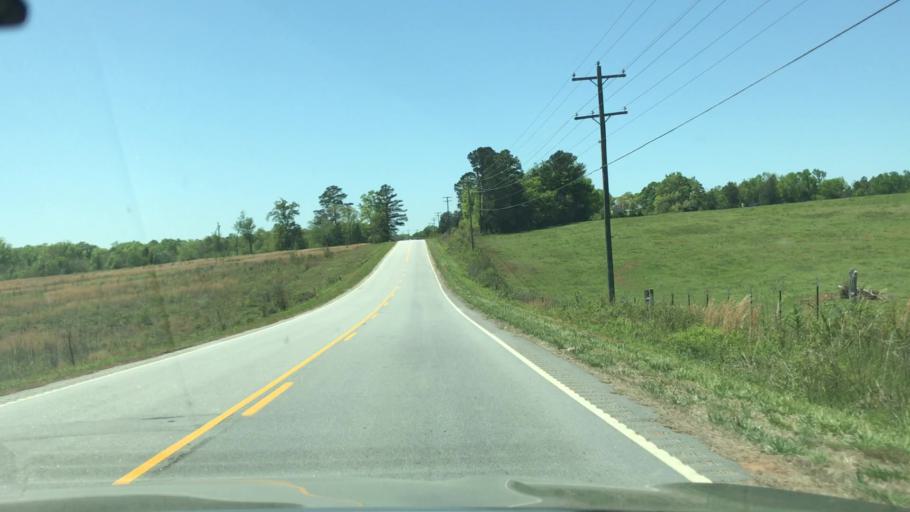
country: US
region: South Carolina
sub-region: Union County
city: Buffalo
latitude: 34.6835
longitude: -81.7169
